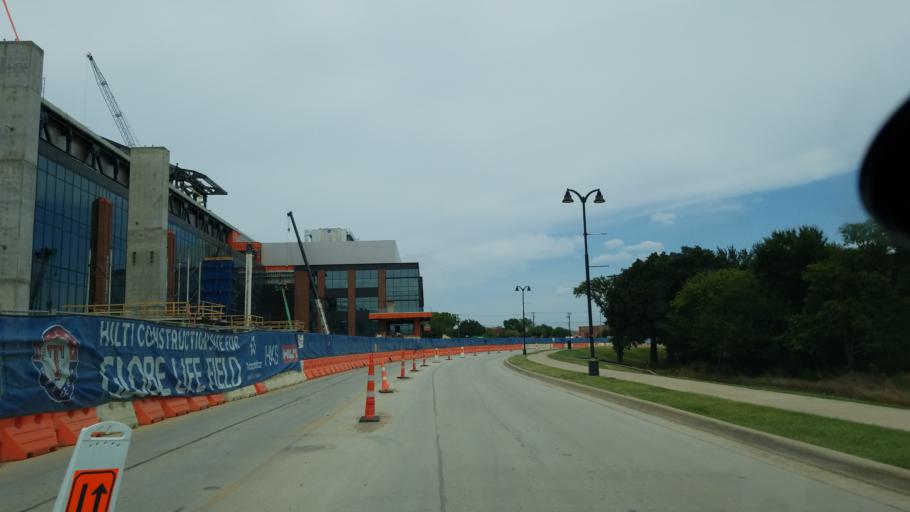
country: US
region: Texas
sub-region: Tarrant County
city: Arlington
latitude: 32.7462
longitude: -97.0858
